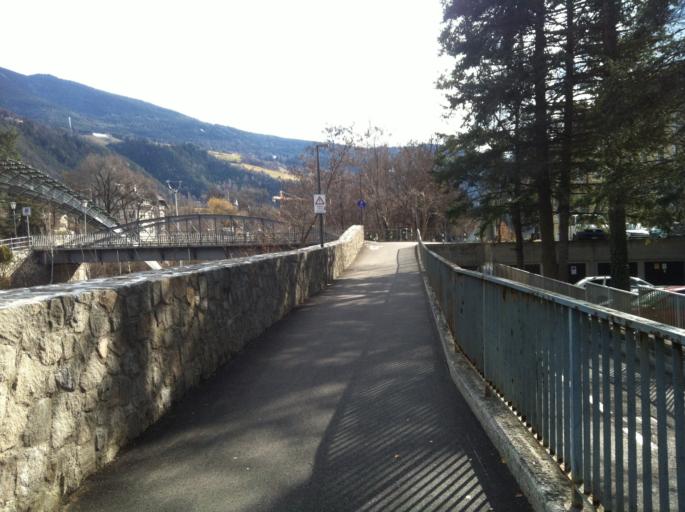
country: IT
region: Trentino-Alto Adige
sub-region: Bolzano
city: Bressanone
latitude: 46.7145
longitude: 11.6606
